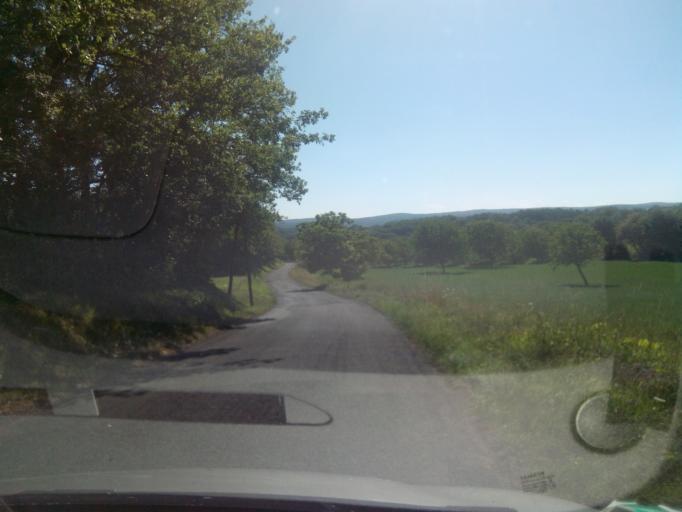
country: FR
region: Limousin
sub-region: Departement de la Correze
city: Meyssac
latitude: 45.0090
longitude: 1.6957
